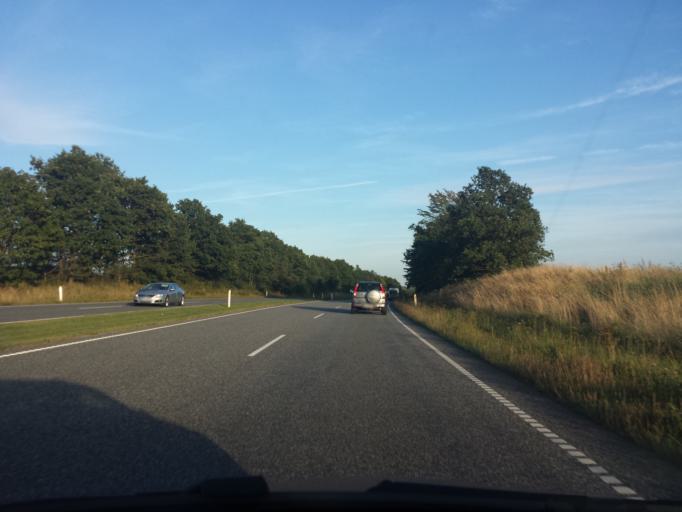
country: DK
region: Capital Region
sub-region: Egedal Kommune
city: Vekso
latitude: 55.7557
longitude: 12.2450
